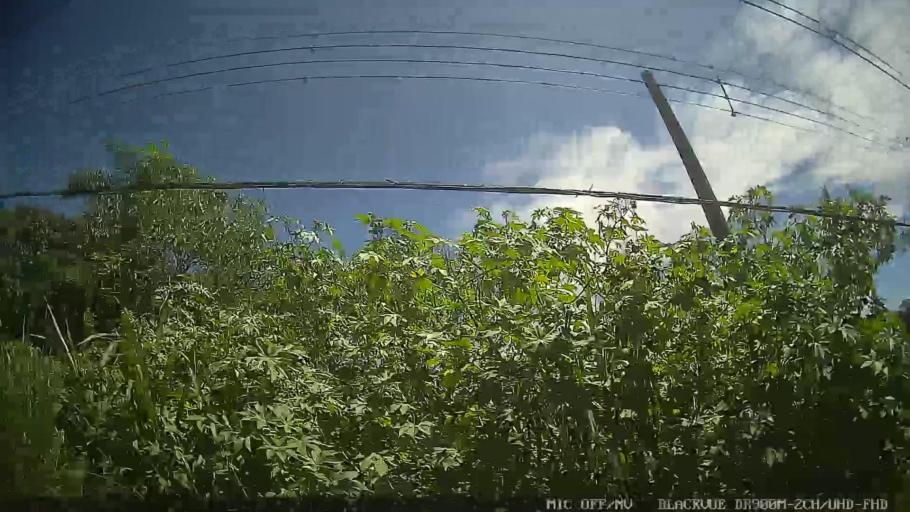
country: BR
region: Sao Paulo
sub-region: Biritiba-Mirim
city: Biritiba Mirim
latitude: -23.5784
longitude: -46.0804
